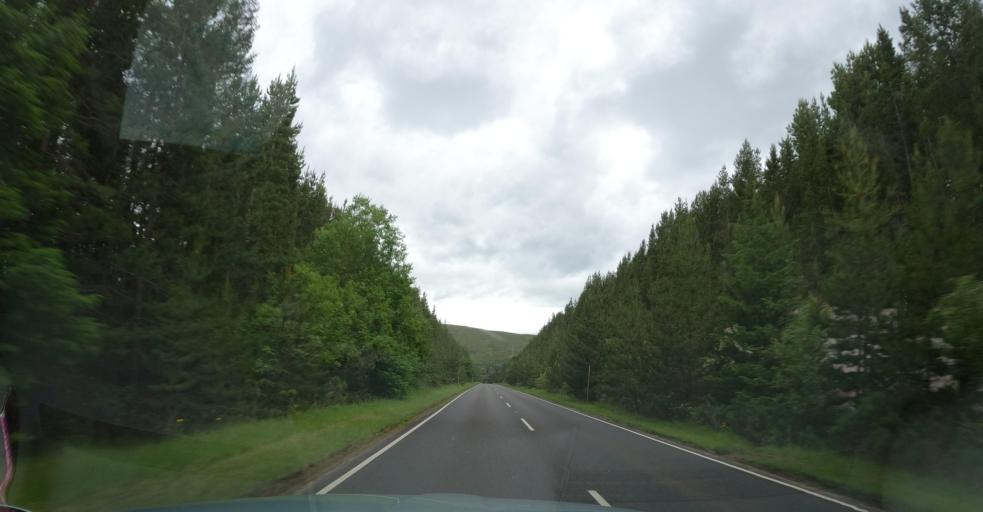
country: GB
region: Scotland
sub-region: Highland
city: Muir of Ord
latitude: 57.6300
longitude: -4.6910
